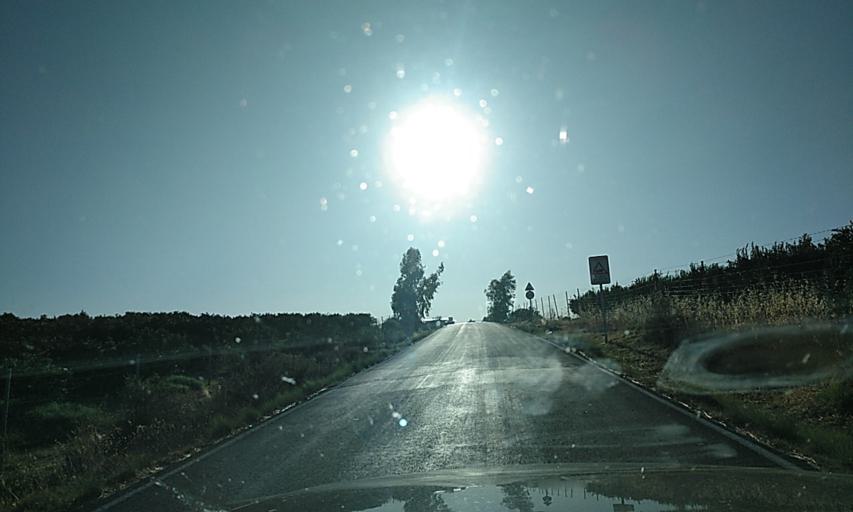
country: ES
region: Andalusia
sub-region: Provincia de Huelva
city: San Bartolome de la Torre
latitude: 37.4138
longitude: -7.1176
